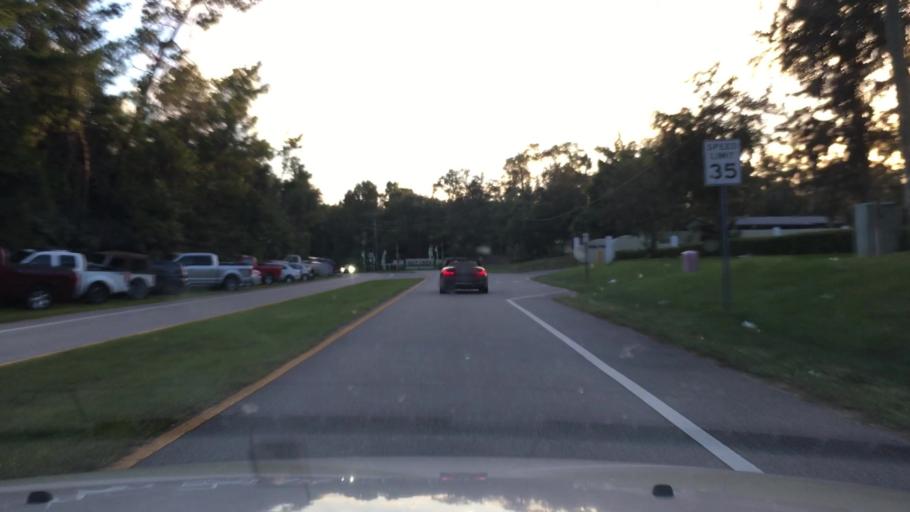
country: US
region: Florida
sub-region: Volusia County
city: Ormond Beach
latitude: 29.3080
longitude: -81.1011
